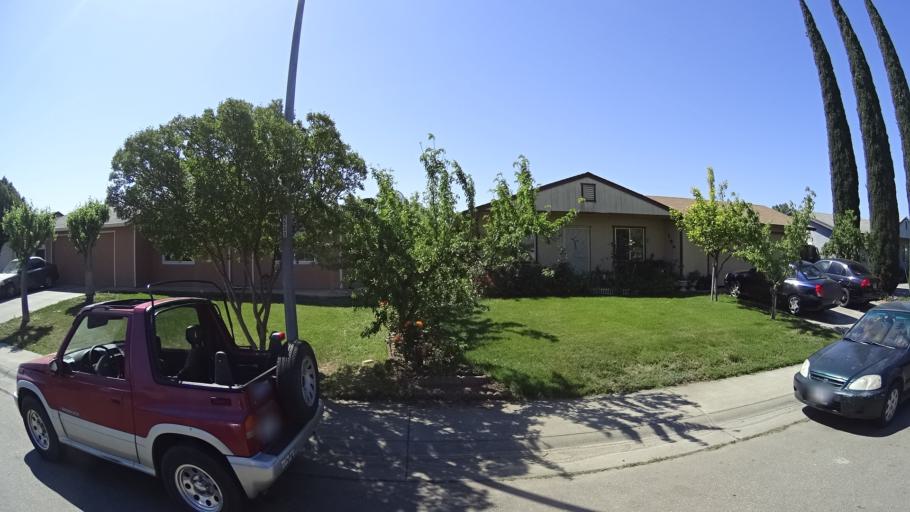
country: US
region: California
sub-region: Glenn County
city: Orland
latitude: 39.7556
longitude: -122.2026
